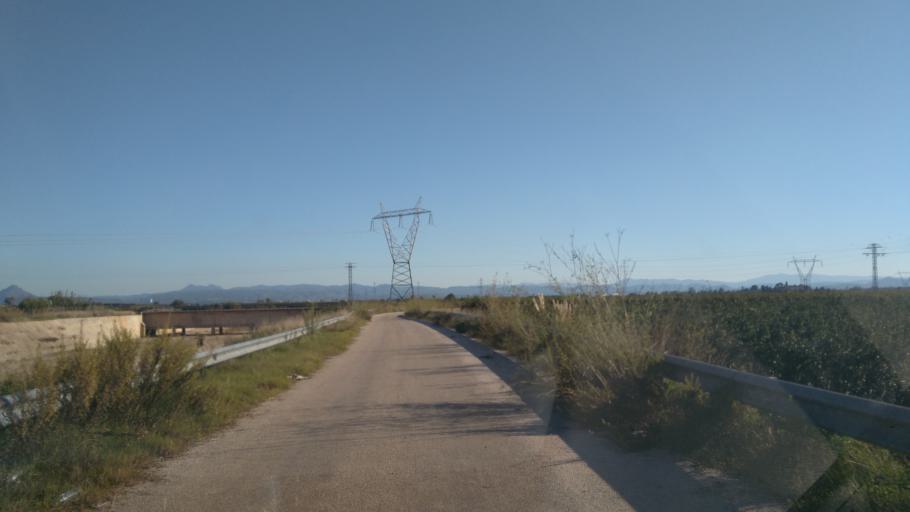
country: ES
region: Valencia
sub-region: Provincia de Valencia
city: L'Alcudia
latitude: 39.1884
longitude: -0.5196
